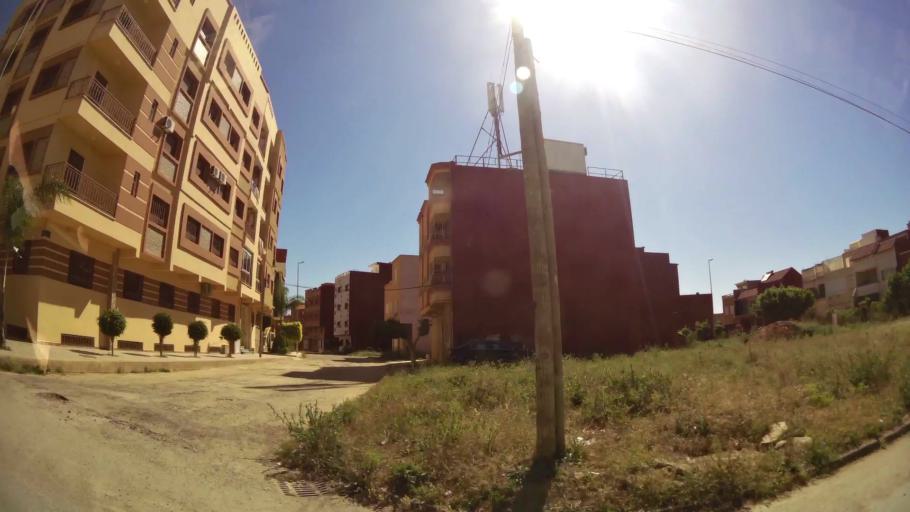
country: MA
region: Oriental
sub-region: Berkane-Taourirt
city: Berkane
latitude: 34.9428
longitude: -2.3323
